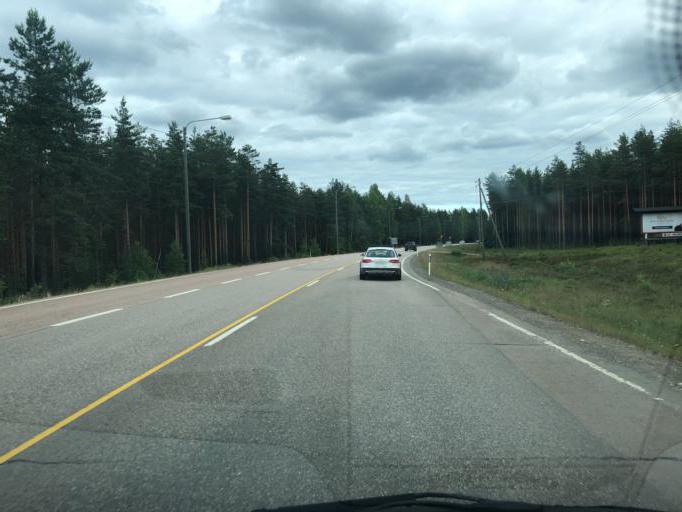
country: FI
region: Southern Savonia
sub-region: Mikkeli
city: Maentyharju
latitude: 61.0915
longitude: 27.0691
